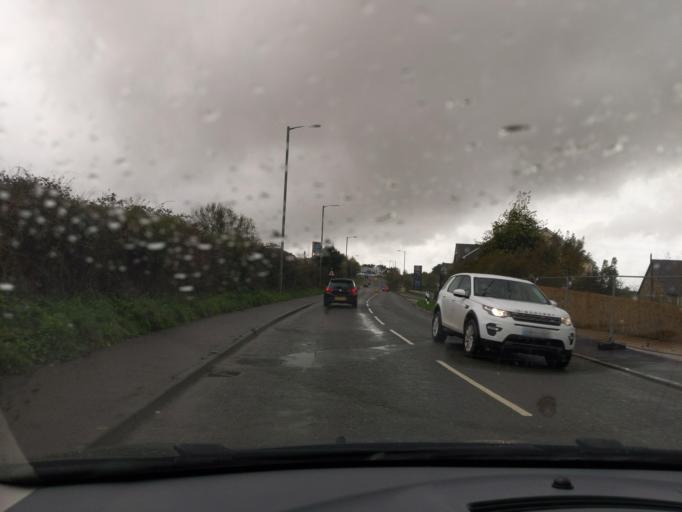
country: GB
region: England
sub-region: Cornwall
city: Wadebridge
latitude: 50.5182
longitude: -4.8530
